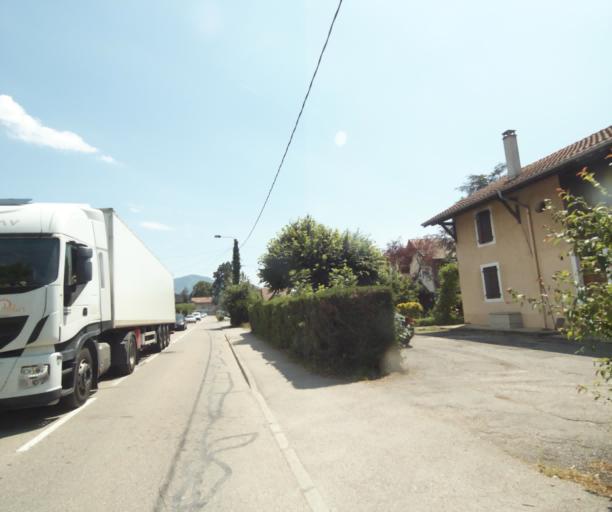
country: FR
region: Rhone-Alpes
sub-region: Departement de la Haute-Savoie
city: Douvaine
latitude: 46.3079
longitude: 6.3030
